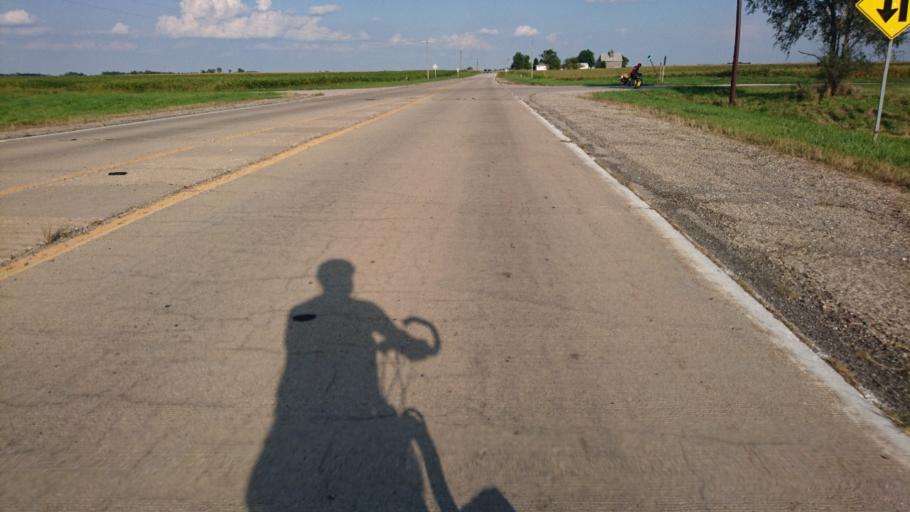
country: US
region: Illinois
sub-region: Logan County
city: Atlanta
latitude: 40.2597
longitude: -89.2152
